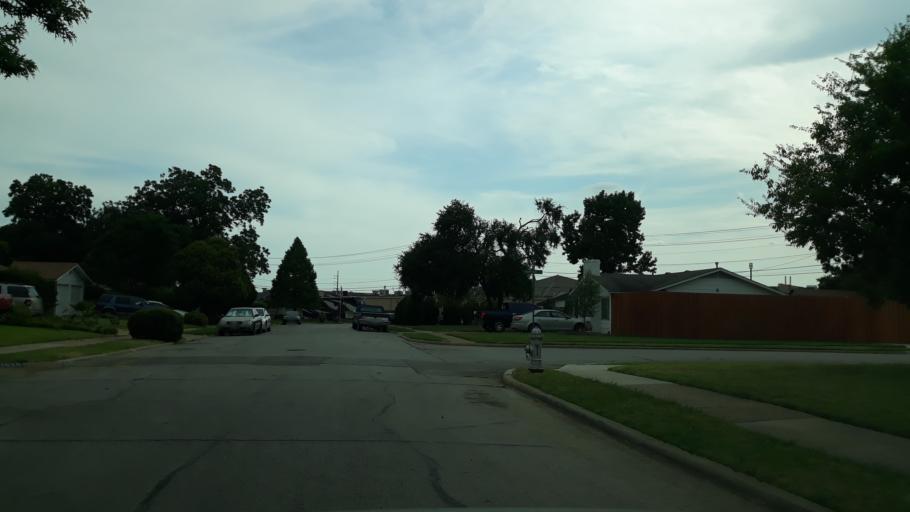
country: US
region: Texas
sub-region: Dallas County
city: Irving
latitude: 32.8429
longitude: -96.9905
